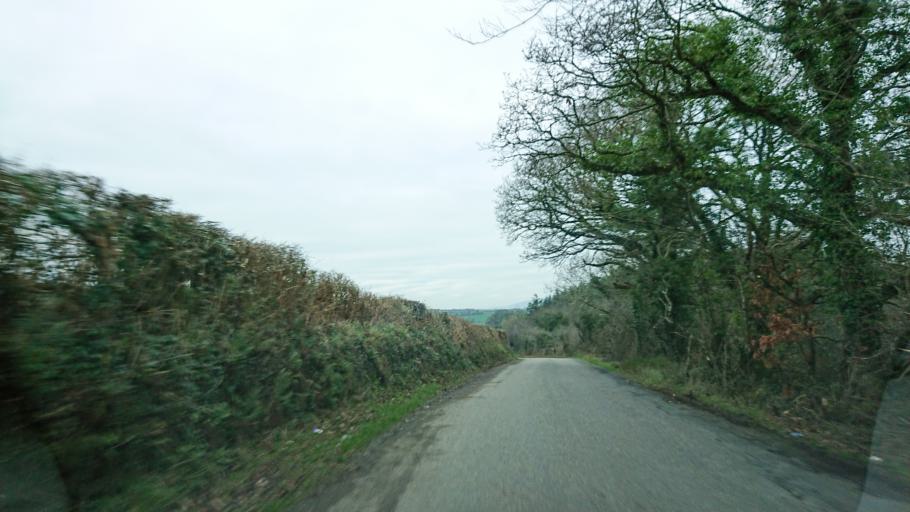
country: IE
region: Munster
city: Carrick-on-Suir
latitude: 52.2744
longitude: -7.4097
